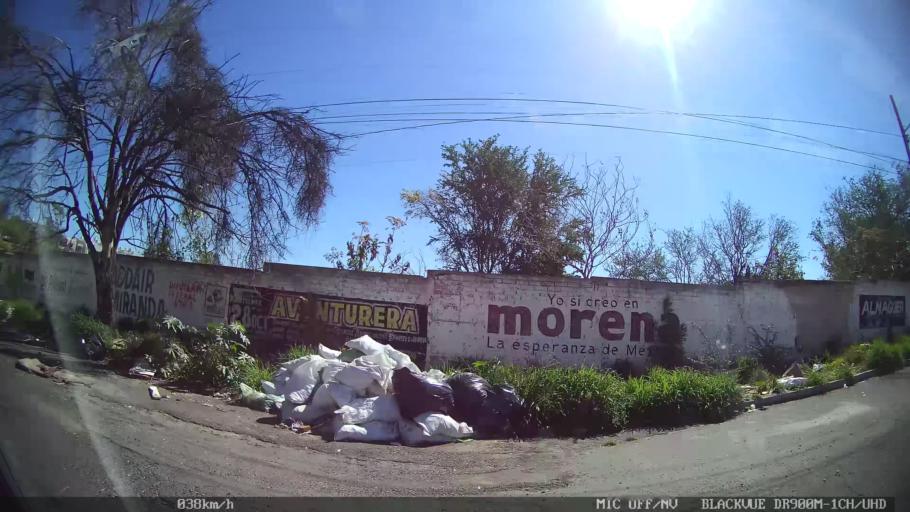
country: MX
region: Jalisco
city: Tlaquepaque
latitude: 20.7029
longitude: -103.2864
